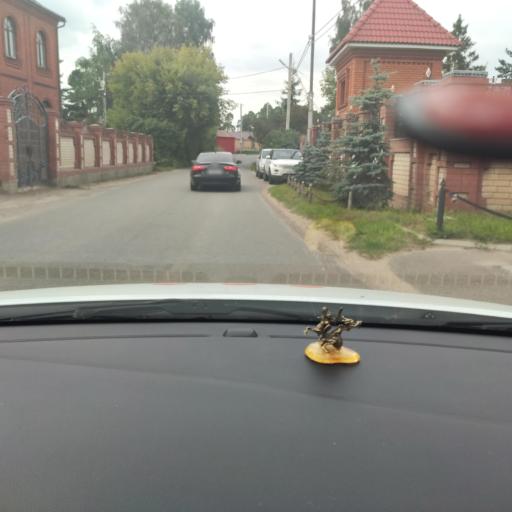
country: RU
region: Tatarstan
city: Verkhniy Uslon
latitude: 55.6181
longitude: 49.0152
